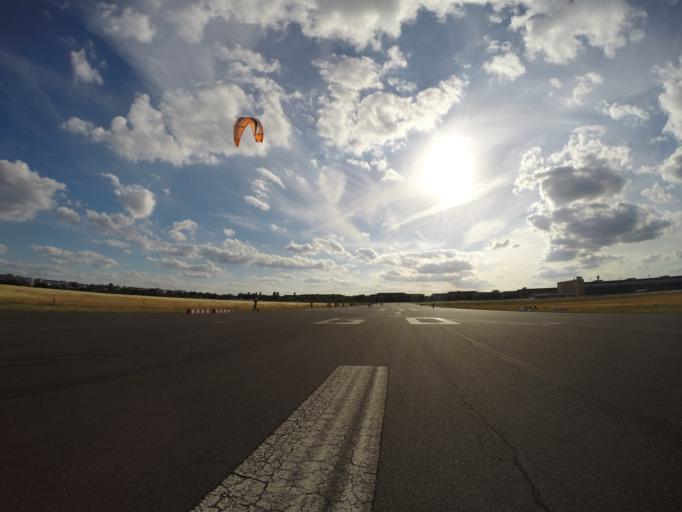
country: DE
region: Berlin
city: Tempelhof Bezirk
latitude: 52.4747
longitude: 13.3950
